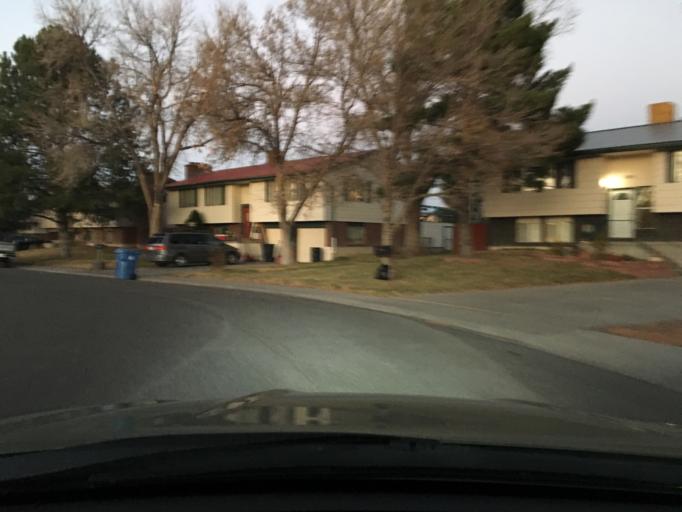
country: US
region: Colorado
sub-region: Montrose County
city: Montrose
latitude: 38.4677
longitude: -107.8578
